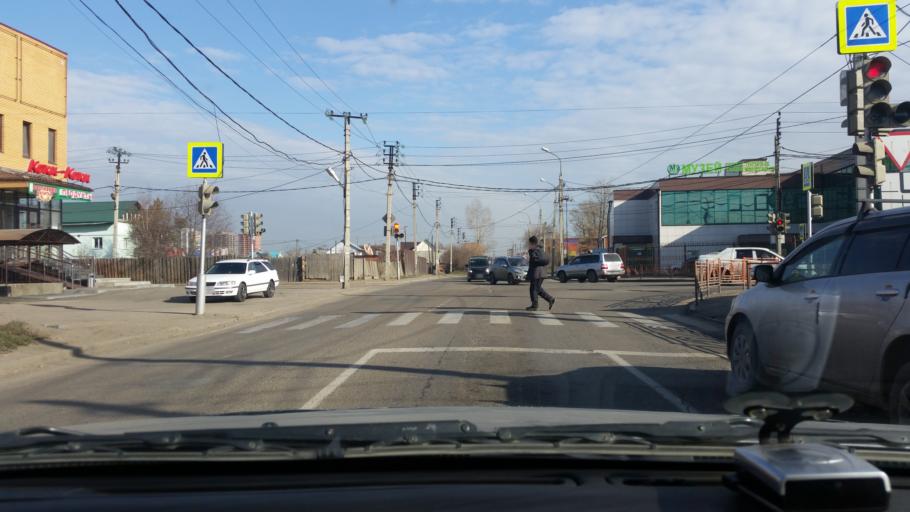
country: RU
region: Irkutsk
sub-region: Irkutskiy Rayon
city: Irkutsk
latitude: 52.2843
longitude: 104.3293
